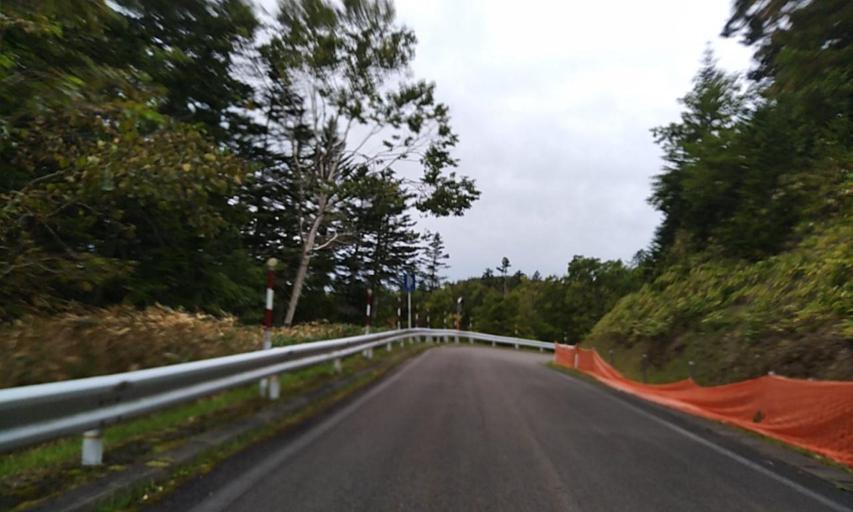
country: JP
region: Hokkaido
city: Bihoro
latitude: 43.5692
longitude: 144.2022
